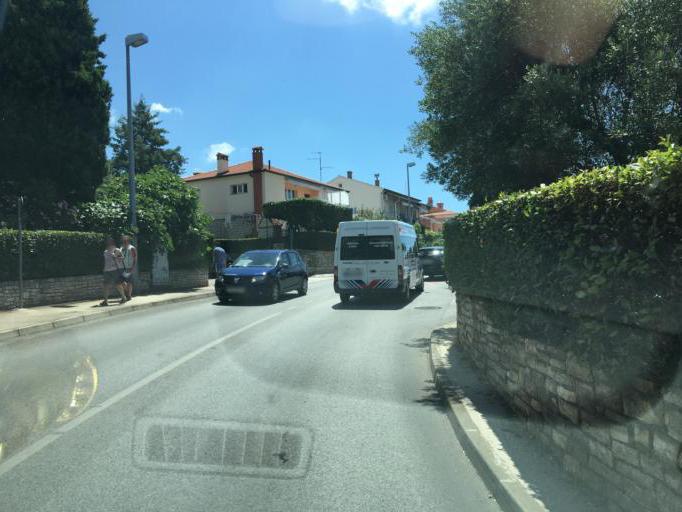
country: HR
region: Istarska
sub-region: Grad Rovinj
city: Rovinj
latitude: 45.0837
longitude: 13.6416
